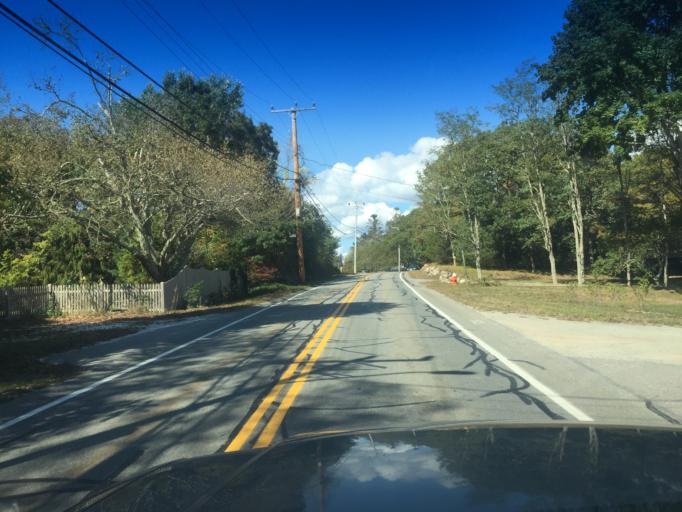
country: US
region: Massachusetts
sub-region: Barnstable County
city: Pocasset
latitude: 41.6680
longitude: -70.6069
